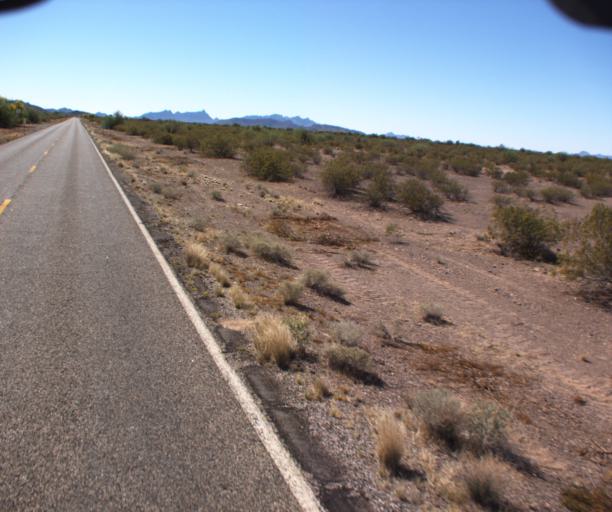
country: US
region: Arizona
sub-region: Pima County
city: Ajo
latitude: 32.3073
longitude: -112.7611
